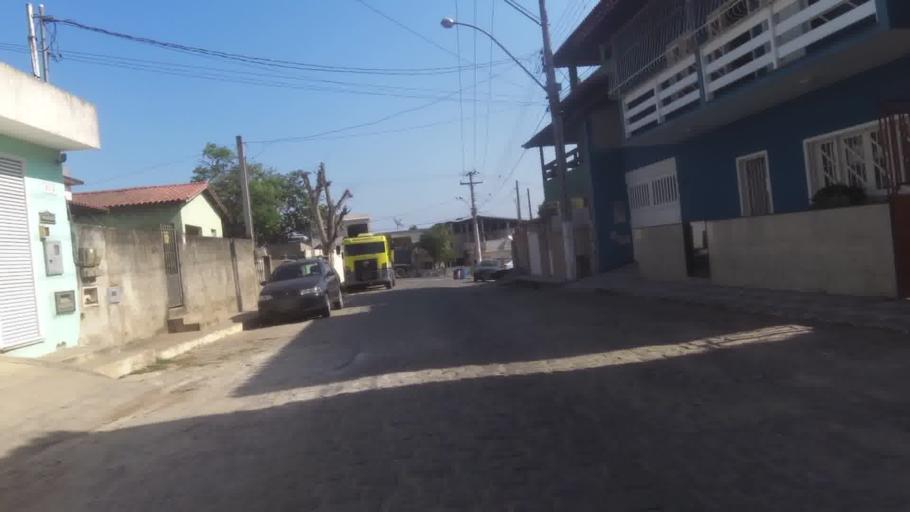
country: BR
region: Espirito Santo
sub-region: Itapemirim
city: Itapemirim
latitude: -21.0093
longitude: -40.8131
